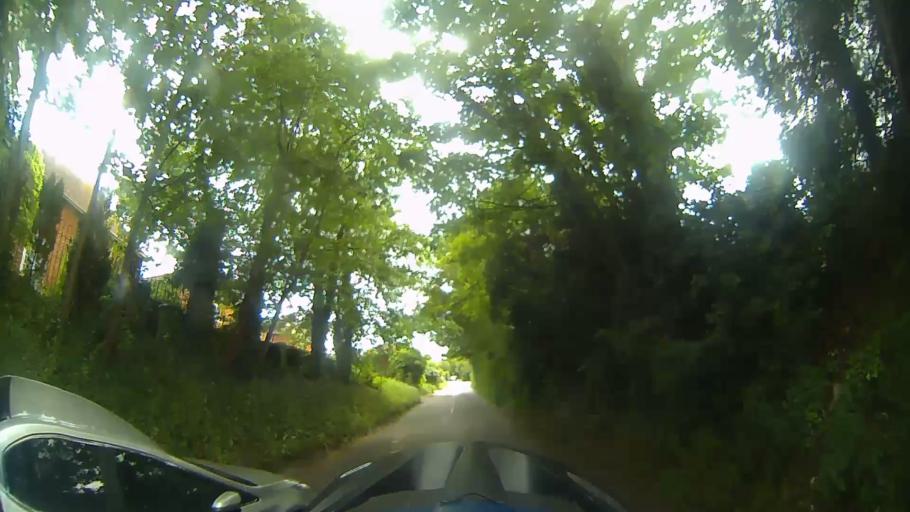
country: GB
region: England
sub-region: Oxfordshire
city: Wantage
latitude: 51.5785
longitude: -1.4502
